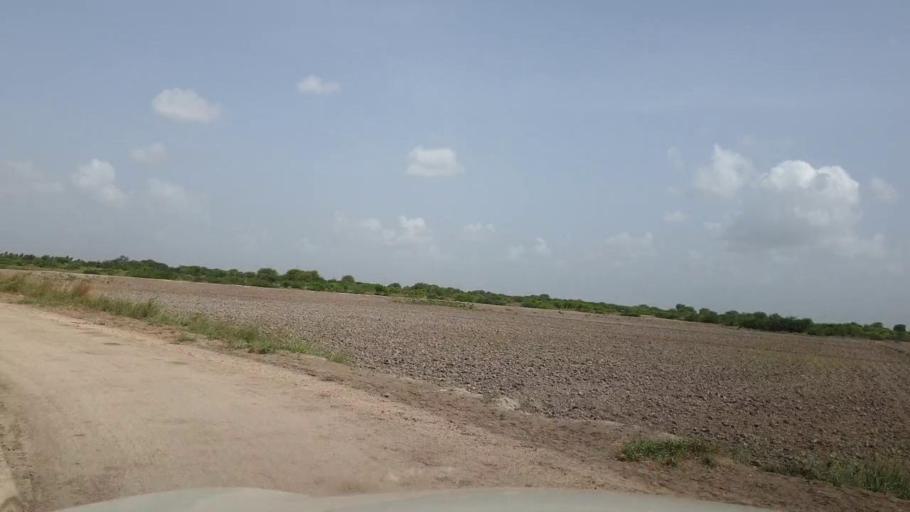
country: PK
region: Sindh
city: Kadhan
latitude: 24.3902
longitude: 68.7951
